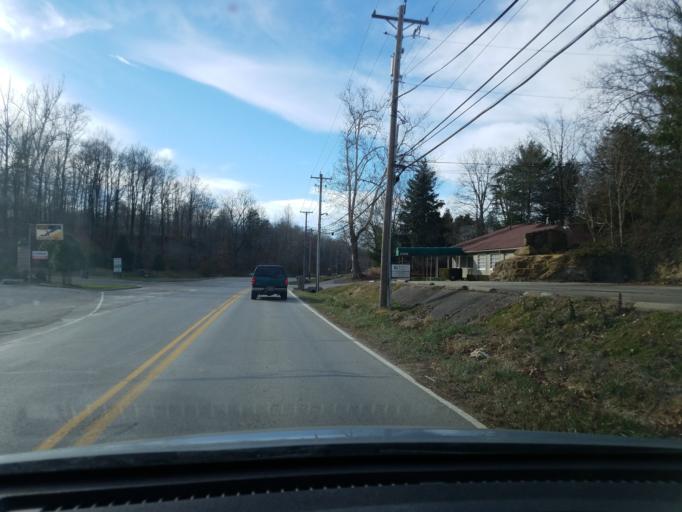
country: US
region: Indiana
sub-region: Floyd County
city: New Albany
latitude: 38.3245
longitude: -85.8632
